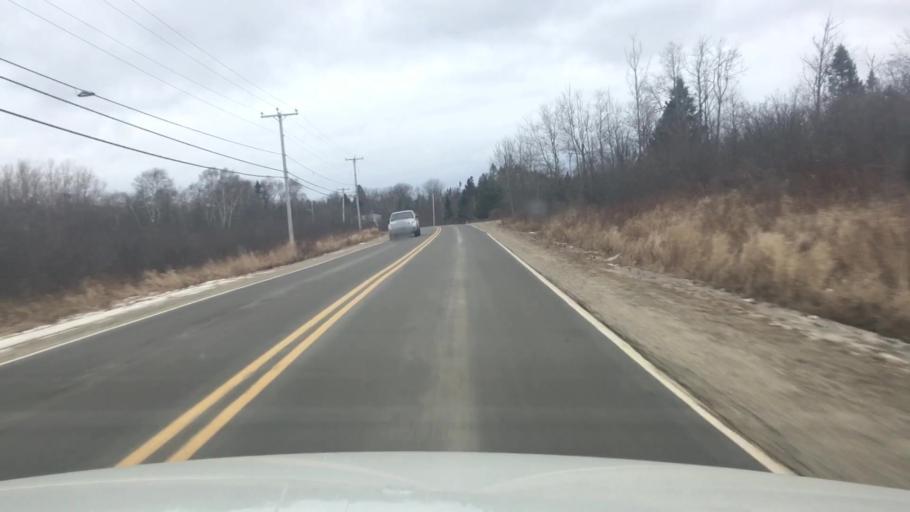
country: US
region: Maine
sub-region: Washington County
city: Jonesport
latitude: 44.5554
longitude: -67.6260
